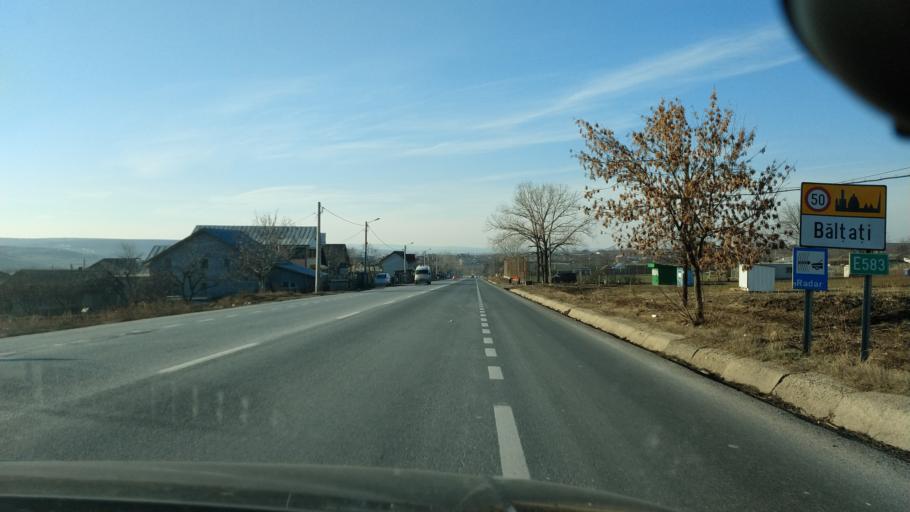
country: RO
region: Iasi
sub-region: Comuna Baltati
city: Baltati
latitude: 47.2203
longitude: 27.1300
